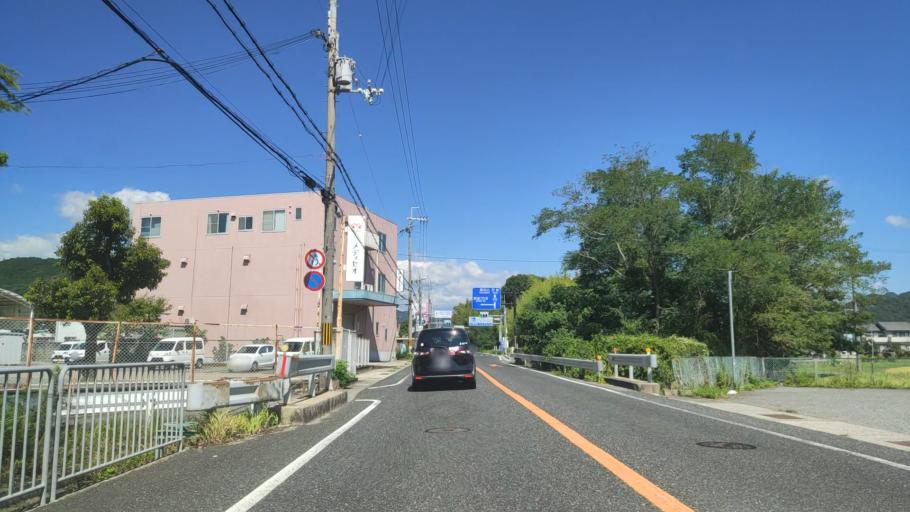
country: JP
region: Hyogo
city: Nishiwaki
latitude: 35.0055
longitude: 134.9921
